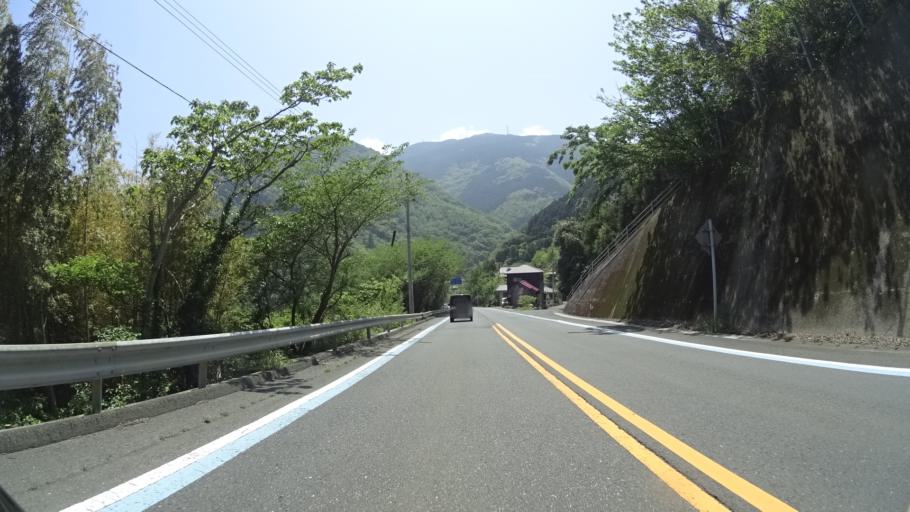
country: JP
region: Ehime
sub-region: Nishiuwa-gun
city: Ikata-cho
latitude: 33.5385
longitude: 132.4046
